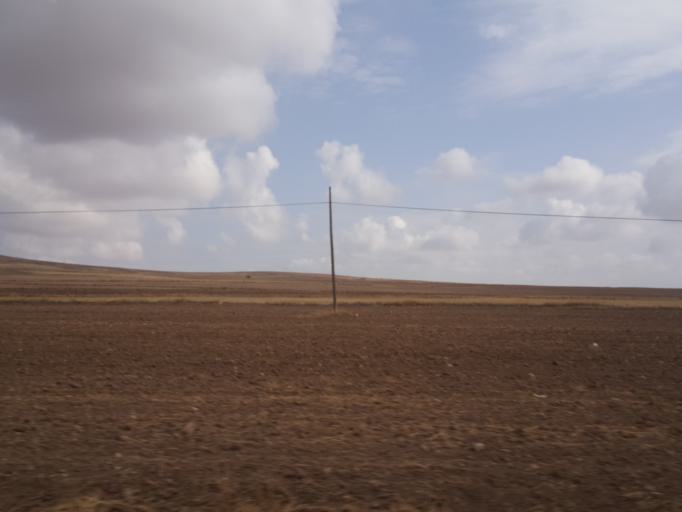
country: TR
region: Kirikkale
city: Keskin
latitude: 39.6231
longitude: 33.6120
